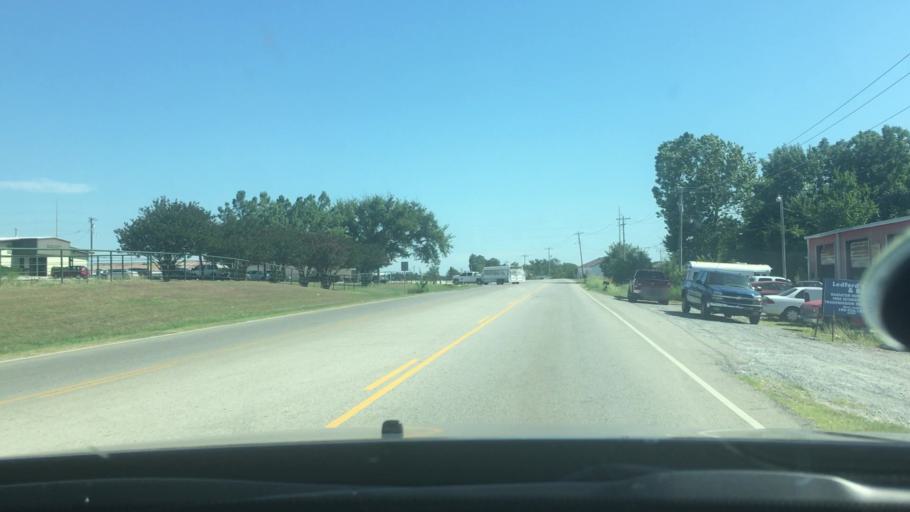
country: US
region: Oklahoma
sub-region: Bryan County
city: Durant
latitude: 33.9711
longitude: -96.3920
